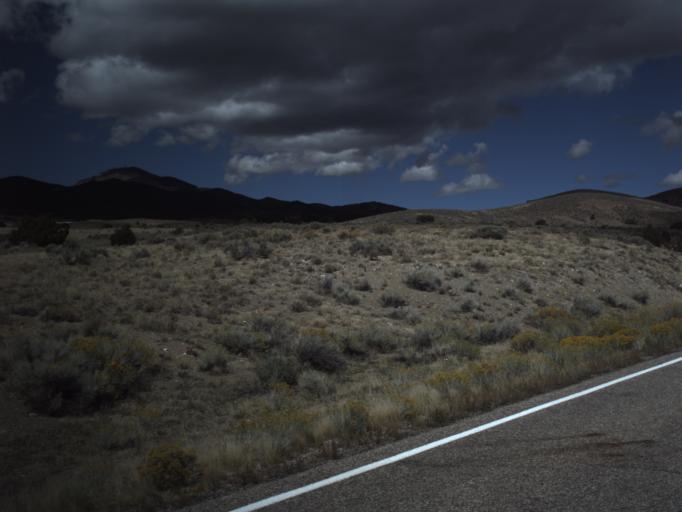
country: US
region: Utah
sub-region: Beaver County
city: Milford
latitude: 38.4408
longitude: -113.2684
